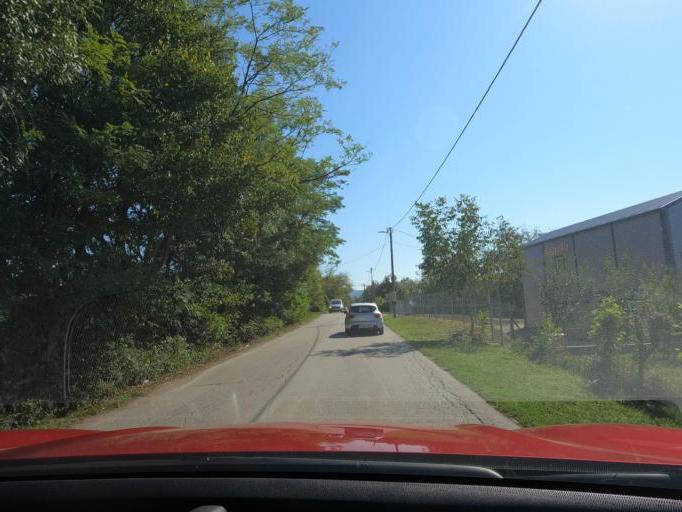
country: RS
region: Central Serbia
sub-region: Raski Okrug
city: Kraljevo
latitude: 43.7547
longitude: 20.6937
